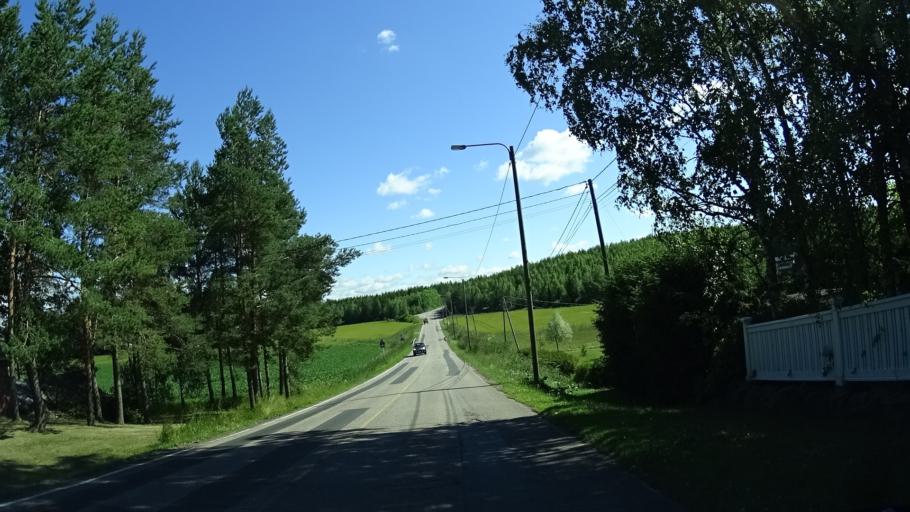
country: FI
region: Varsinais-Suomi
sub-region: Turku
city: Askainen
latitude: 60.5718
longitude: 21.9070
